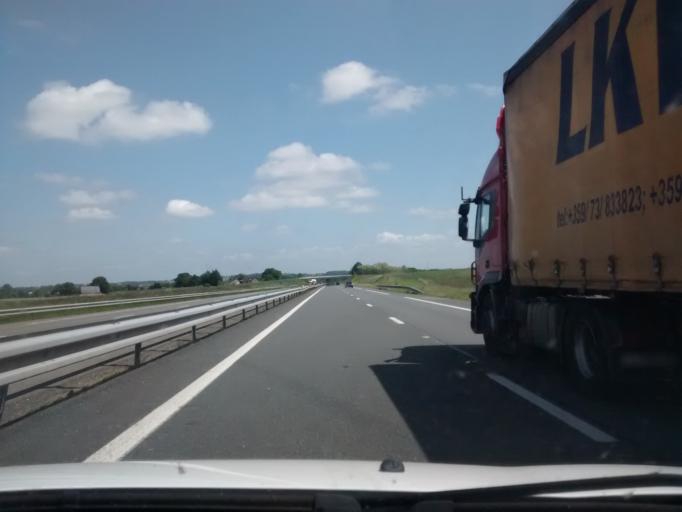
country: FR
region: Pays de la Loire
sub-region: Departement de la Sarthe
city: Louplande
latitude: 48.0137
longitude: -0.0840
